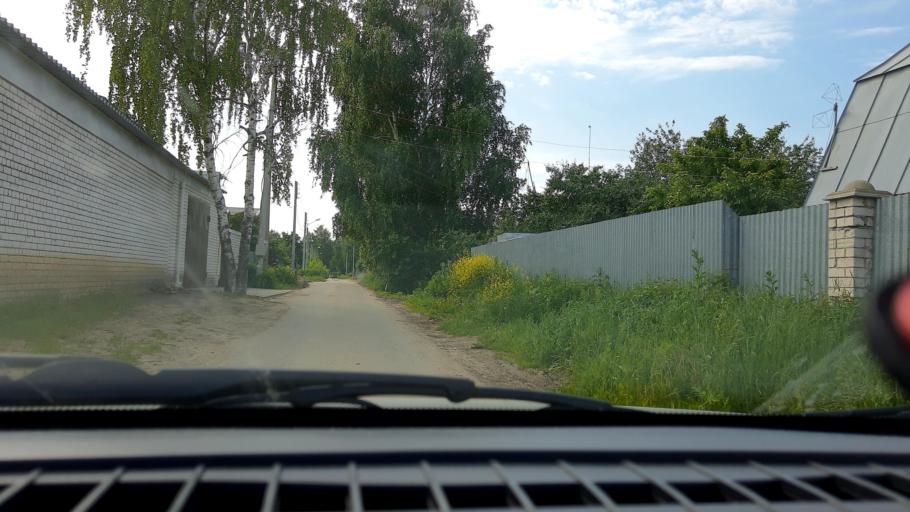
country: RU
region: Nizjnij Novgorod
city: Nizhniy Novgorod
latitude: 56.3041
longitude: 43.8742
